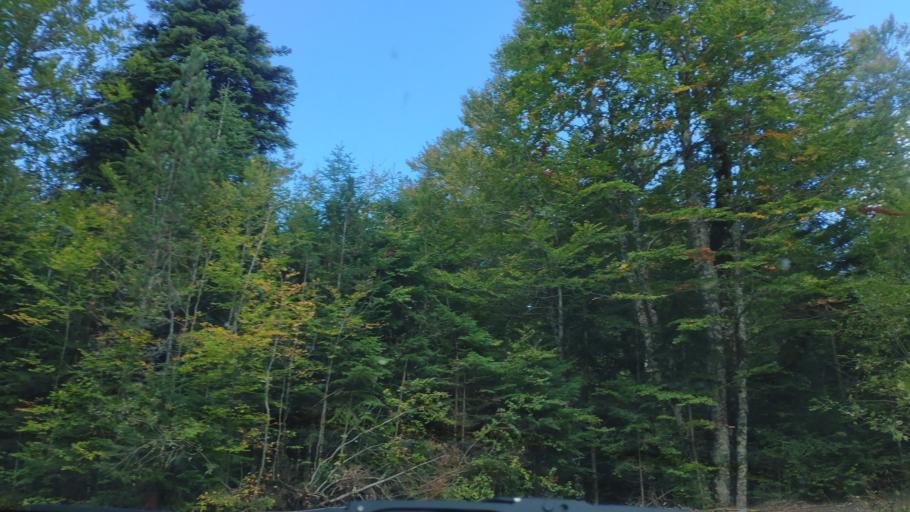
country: AL
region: Korce
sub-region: Rrethi i Devollit
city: Miras
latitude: 40.3354
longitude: 20.9002
